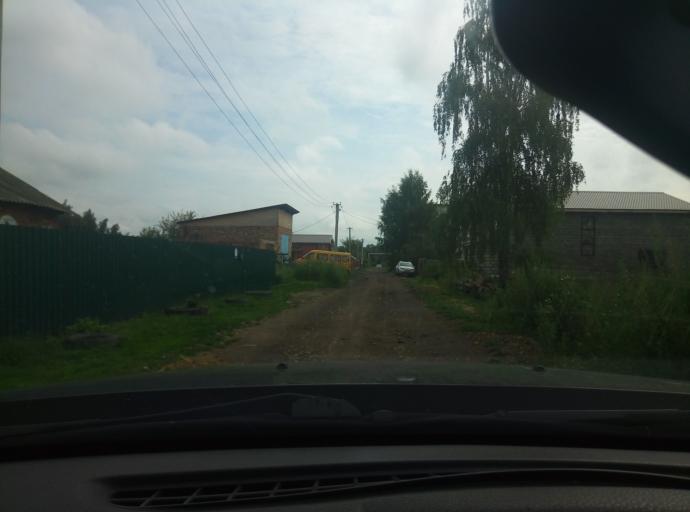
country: RU
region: Tula
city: Kimovsk
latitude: 53.9756
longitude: 38.5231
